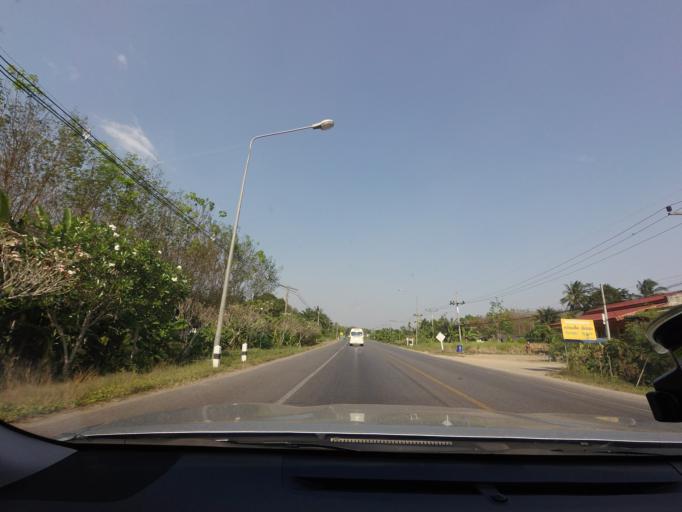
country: TH
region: Surat Thani
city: Phrasaeng
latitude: 8.5726
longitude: 99.2071
